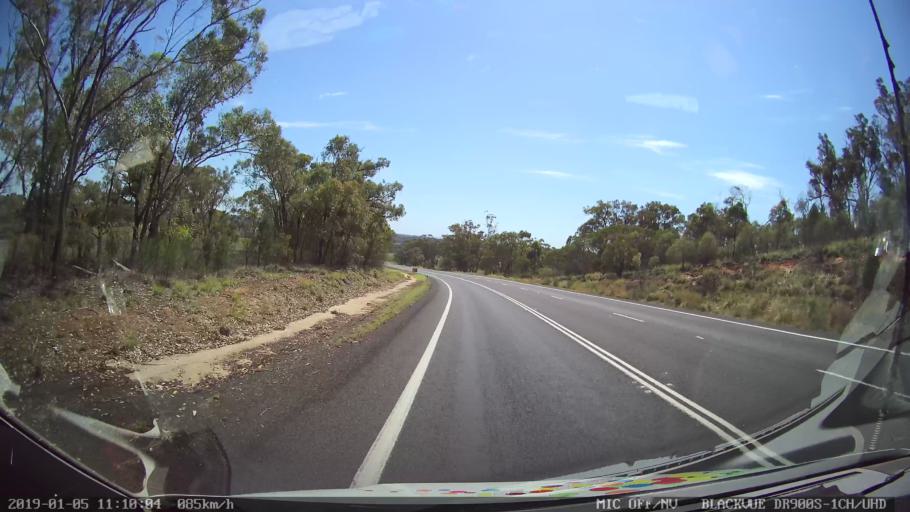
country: AU
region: New South Wales
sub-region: Warrumbungle Shire
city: Coonabarabran
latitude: -31.4100
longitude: 149.2406
